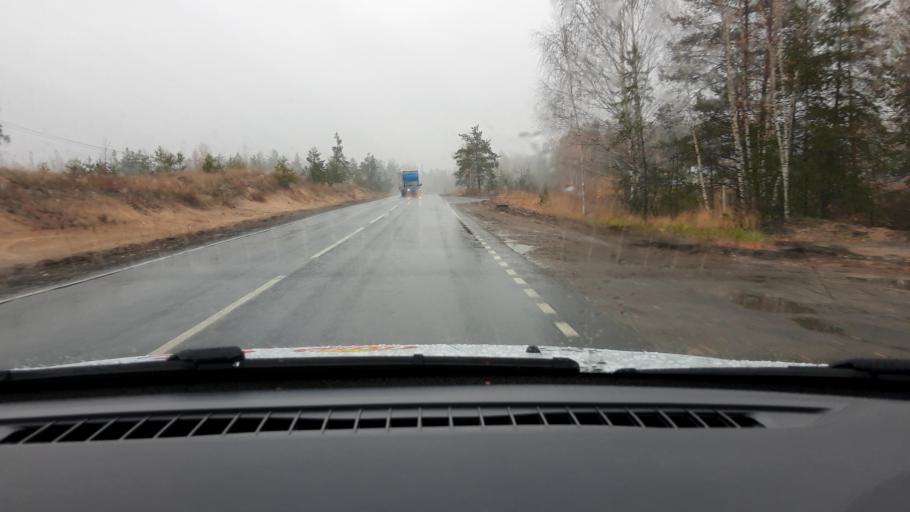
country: RU
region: Nizjnij Novgorod
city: Babino
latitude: 56.2764
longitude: 43.5944
